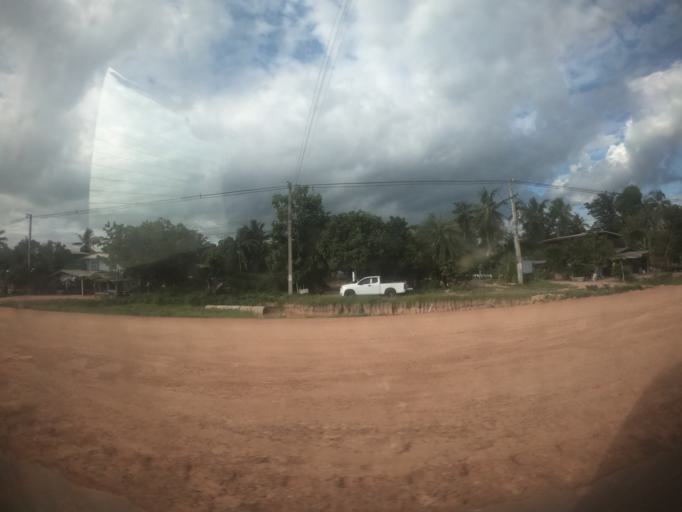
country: TH
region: Surin
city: Kap Choeng
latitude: 14.4897
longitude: 103.5752
